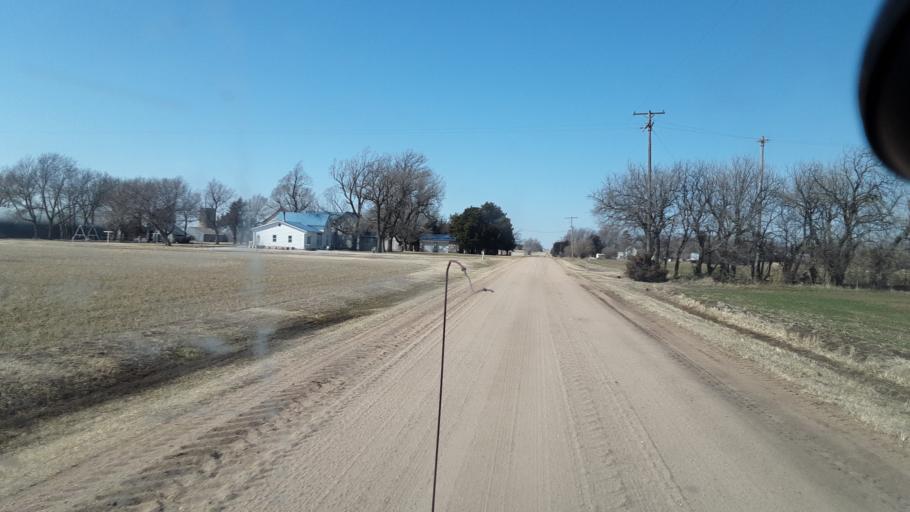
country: US
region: Kansas
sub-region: Reno County
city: South Hutchinson
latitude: 37.9846
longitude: -98.0267
